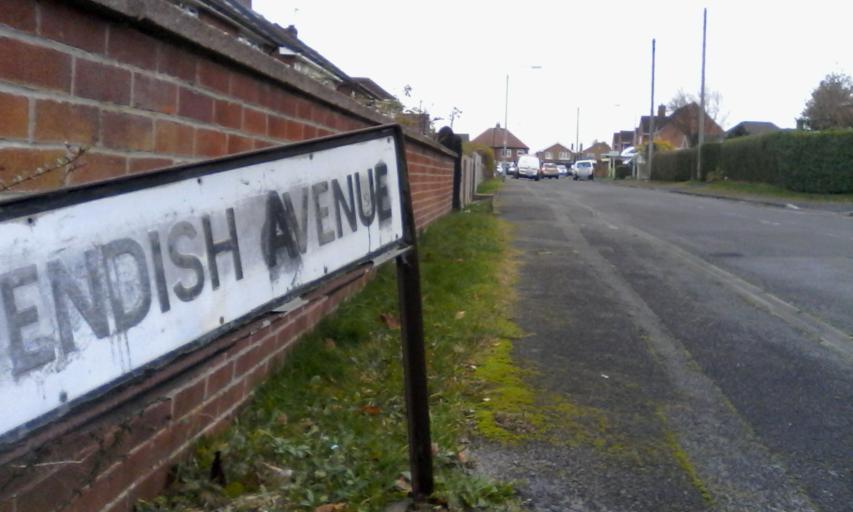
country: GB
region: England
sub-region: Nottinghamshire
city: Arnold
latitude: 52.9801
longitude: -1.0982
